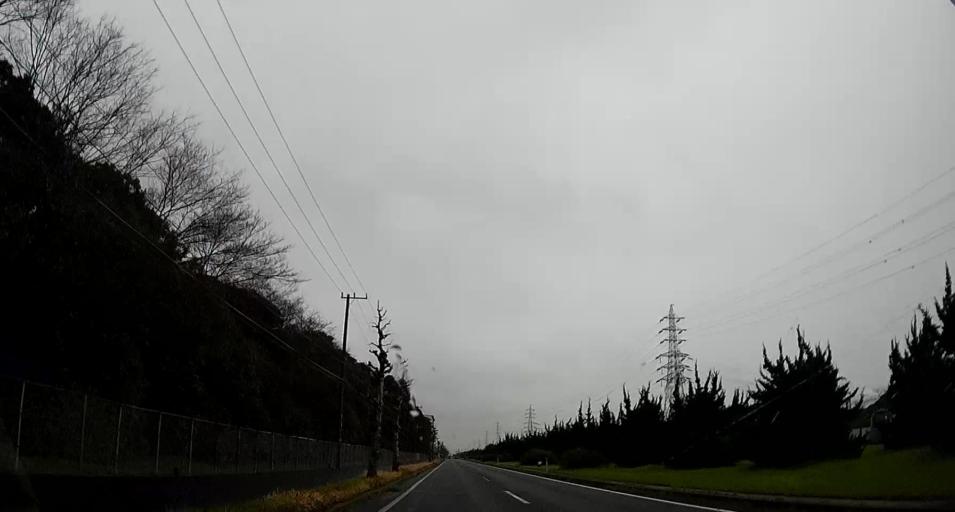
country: JP
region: Chiba
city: Ichihara
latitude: 35.5112
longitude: 140.0561
